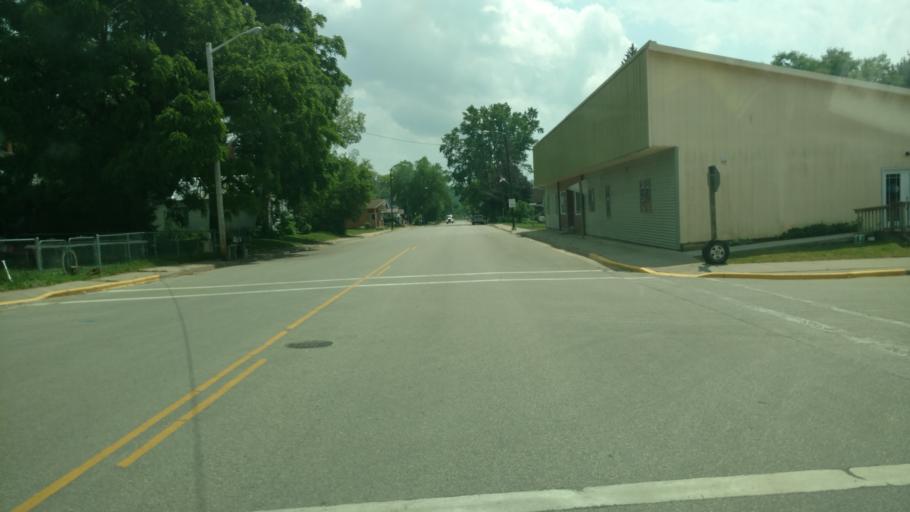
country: US
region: Wisconsin
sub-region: Vernon County
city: Viroqua
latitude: 43.4512
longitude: -90.7592
